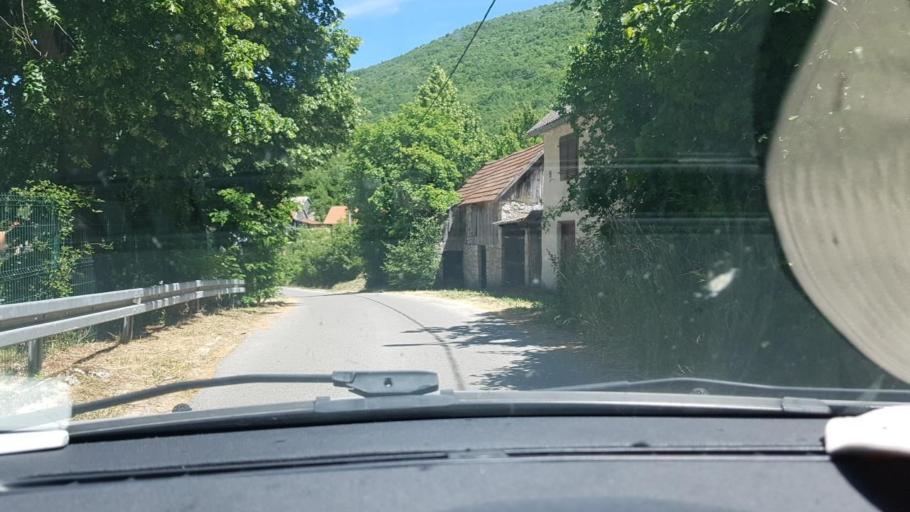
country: HR
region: Licko-Senjska
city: Otocac
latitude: 44.7869
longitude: 15.3675
